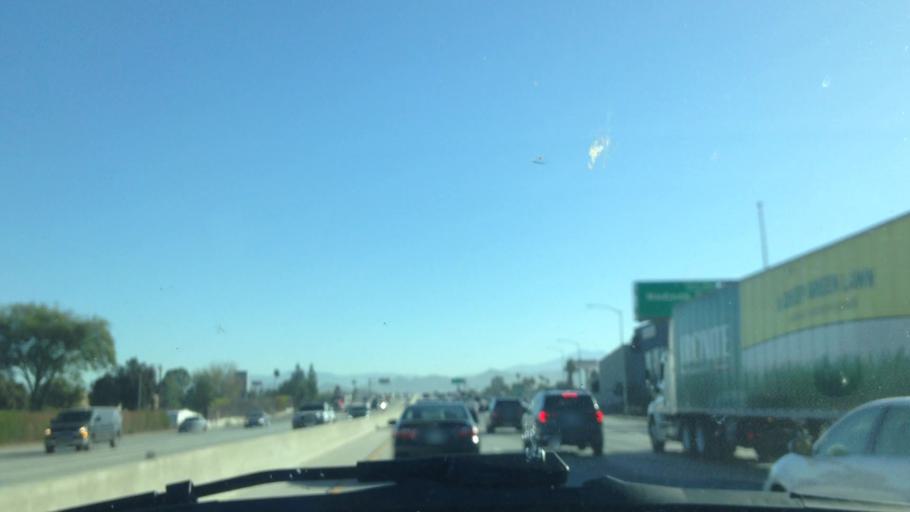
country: US
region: California
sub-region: Riverside County
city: Riverside
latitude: 33.9336
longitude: -117.4078
